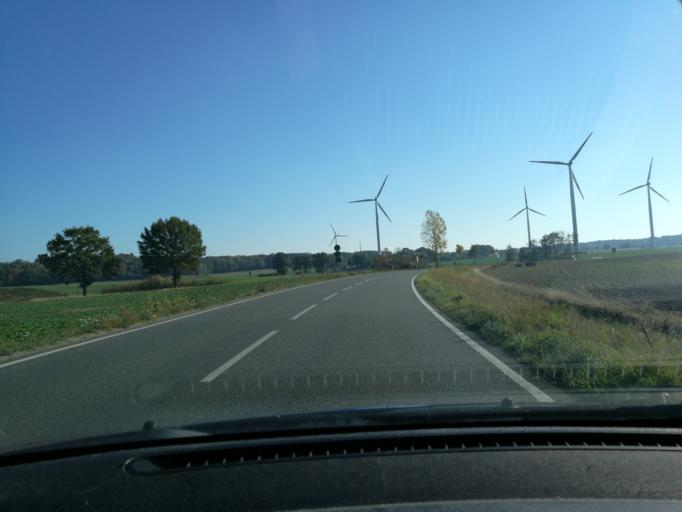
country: DE
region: Lower Saxony
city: Barendorf
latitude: 53.2214
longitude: 10.5190
